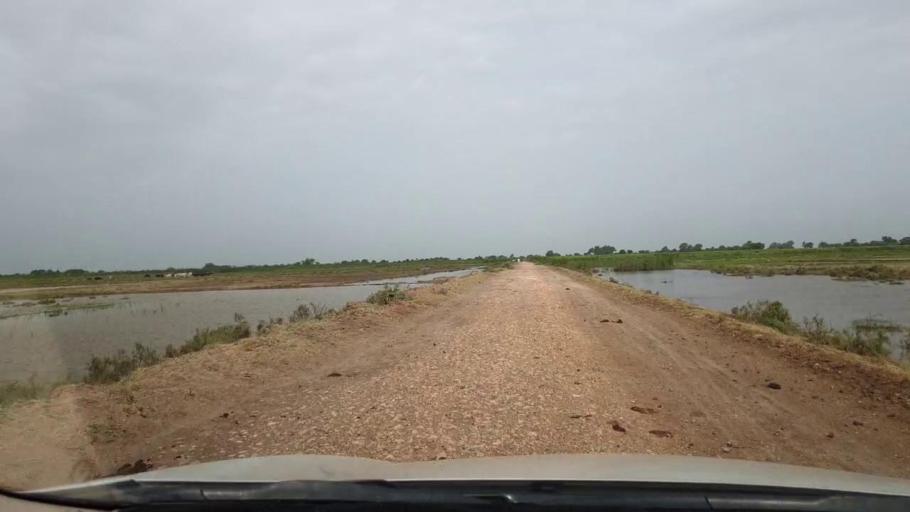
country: PK
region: Sindh
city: Matli
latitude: 25.1036
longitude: 68.6239
